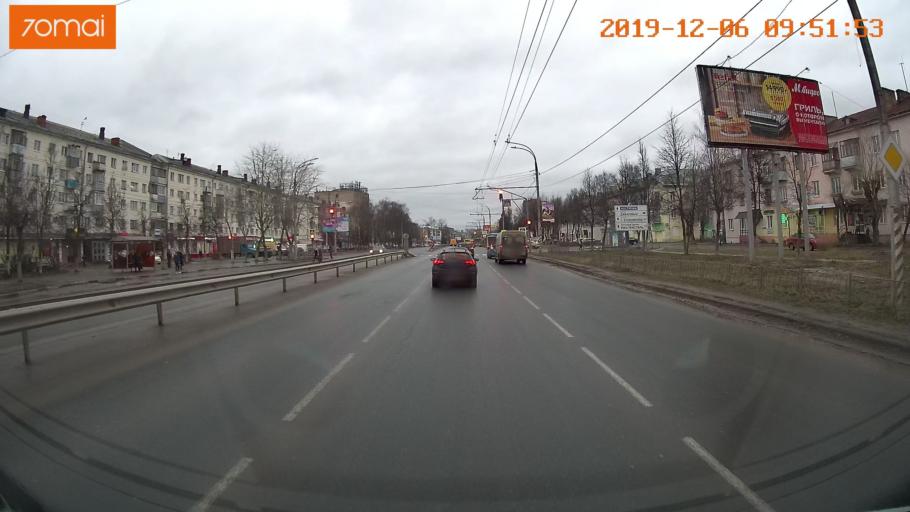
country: RU
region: Ivanovo
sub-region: Gorod Ivanovo
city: Ivanovo
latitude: 56.9664
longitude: 40.9735
